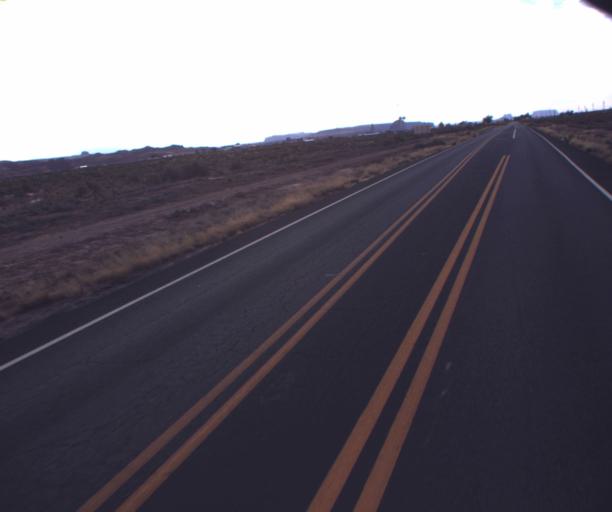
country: US
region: Arizona
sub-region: Apache County
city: Many Farms
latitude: 36.7285
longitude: -109.6311
